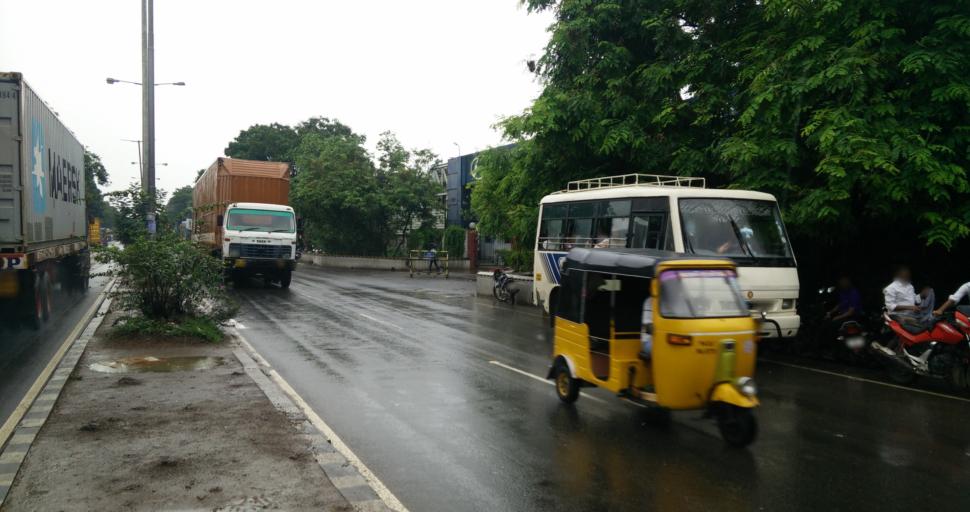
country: IN
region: Tamil Nadu
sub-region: Kancheepuram
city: Sriperumbudur
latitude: 13.0029
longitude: 79.9976
